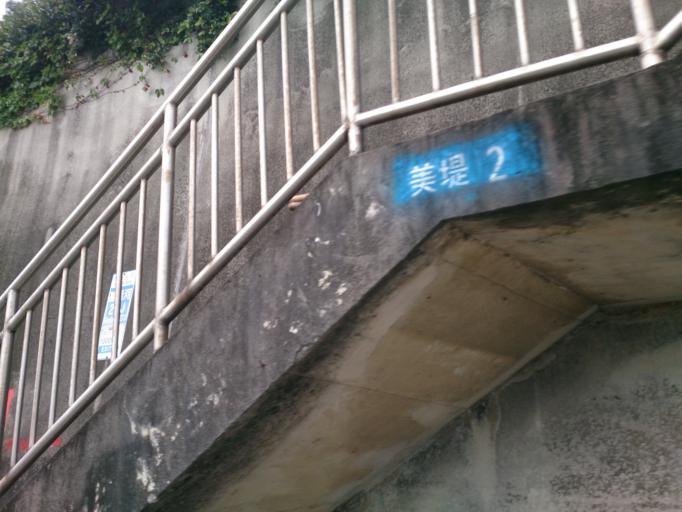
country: TW
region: Taipei
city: Taipei
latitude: 25.0761
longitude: 121.5710
